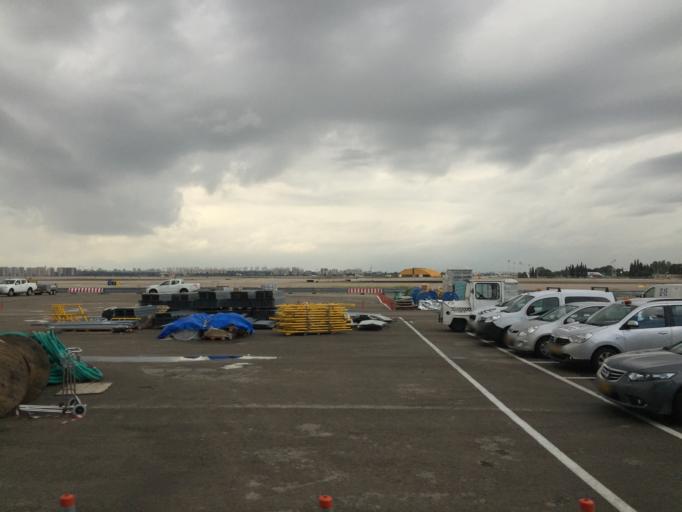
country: IL
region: Central District
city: Yehud
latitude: 31.9959
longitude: 34.8953
